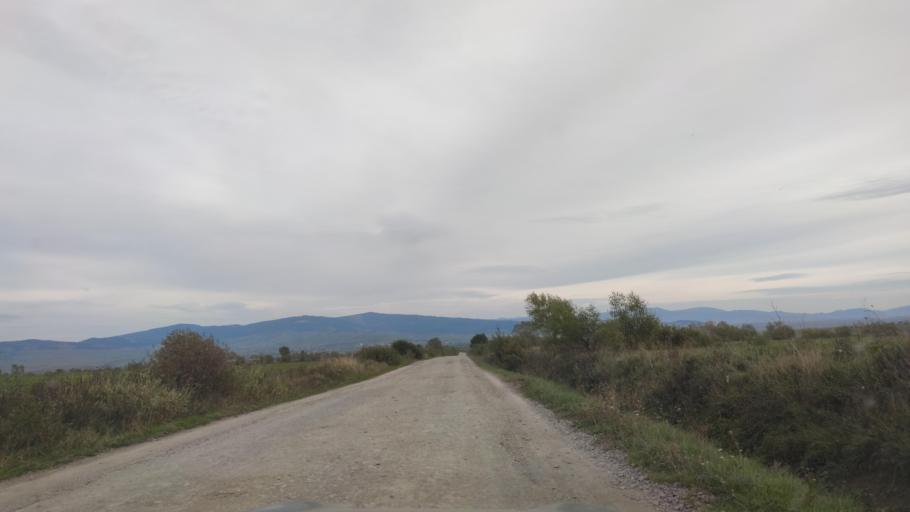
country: RO
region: Harghita
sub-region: Comuna Remetea
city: Remetea
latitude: 46.8100
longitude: 25.3959
